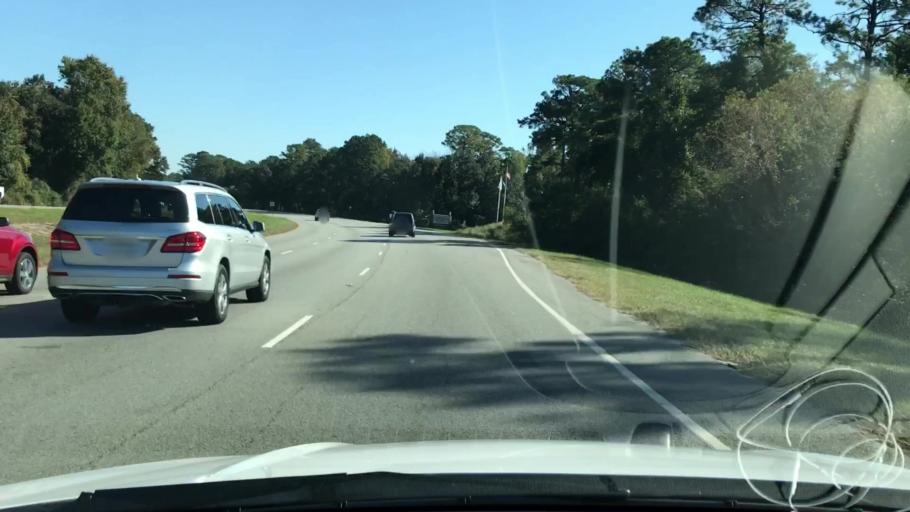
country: US
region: South Carolina
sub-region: Beaufort County
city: Bluffton
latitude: 32.2416
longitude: -80.8228
